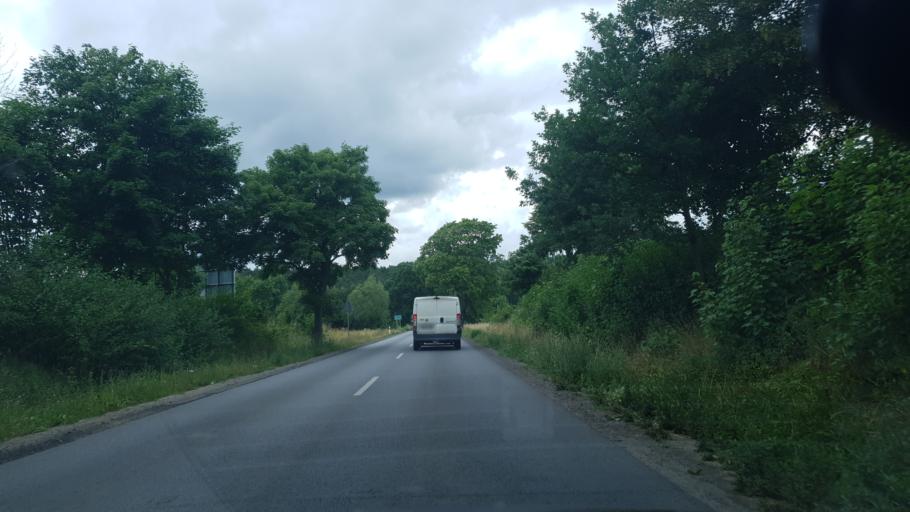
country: PL
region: Pomeranian Voivodeship
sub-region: Powiat kartuski
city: Zukowo
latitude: 54.3840
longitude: 18.3453
